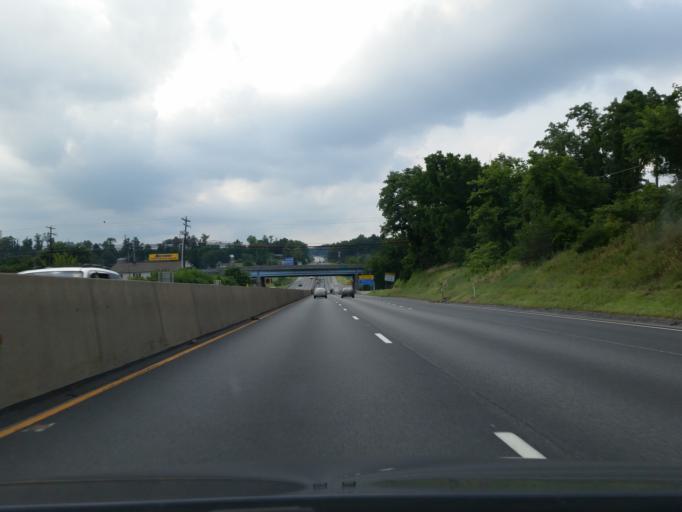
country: US
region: Pennsylvania
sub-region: York County
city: Valley Green
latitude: 40.1651
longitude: -76.8282
